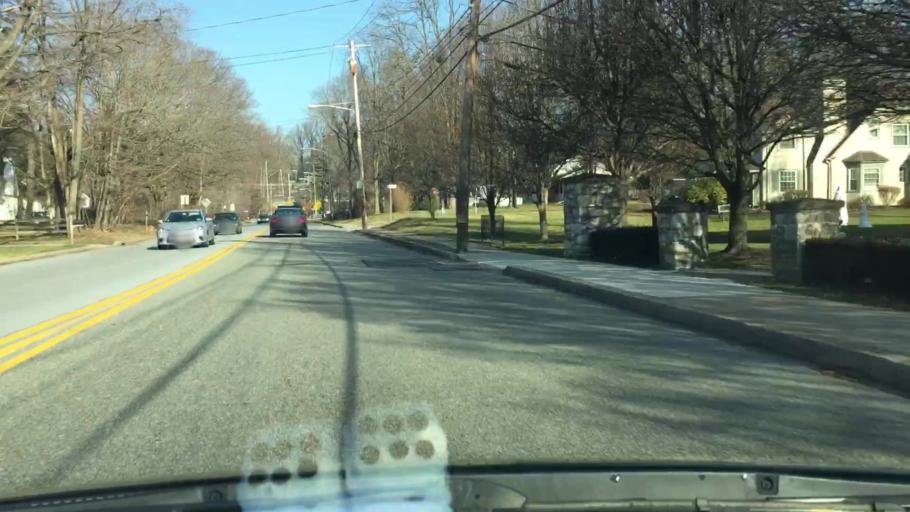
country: US
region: Pennsylvania
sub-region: Delaware County
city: Wayne
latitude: 40.0471
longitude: -75.4043
